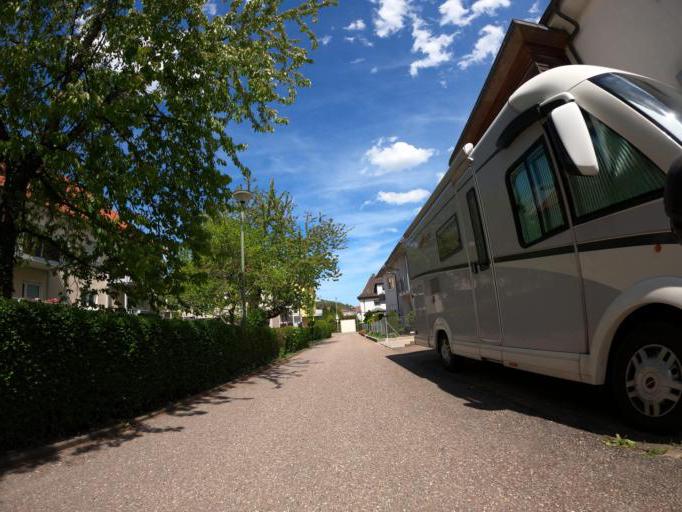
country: DE
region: Baden-Wuerttemberg
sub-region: Karlsruhe Region
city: Birkenfeld
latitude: 48.8853
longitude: 8.6565
